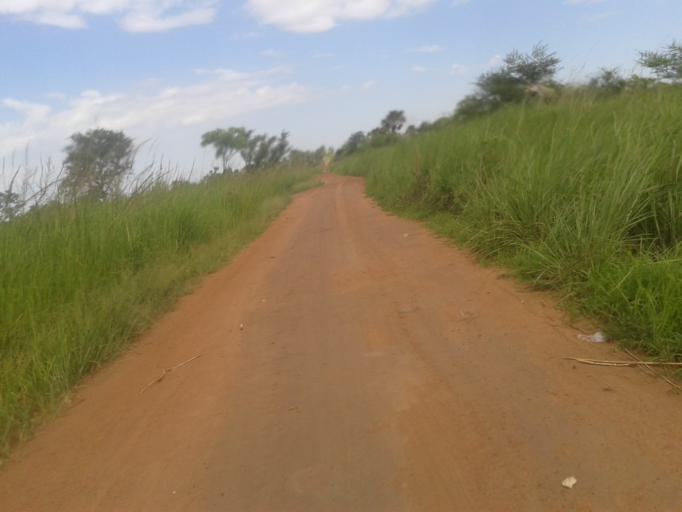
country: UG
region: Northern Region
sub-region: Gulu District
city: Gulu
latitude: 2.8278
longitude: 32.2368
